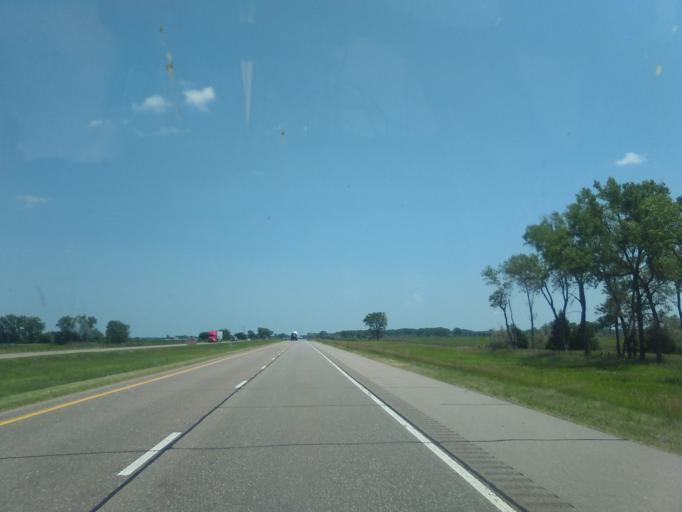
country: US
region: Nebraska
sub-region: Dawson County
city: Cozad
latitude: 40.8742
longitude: -100.0570
